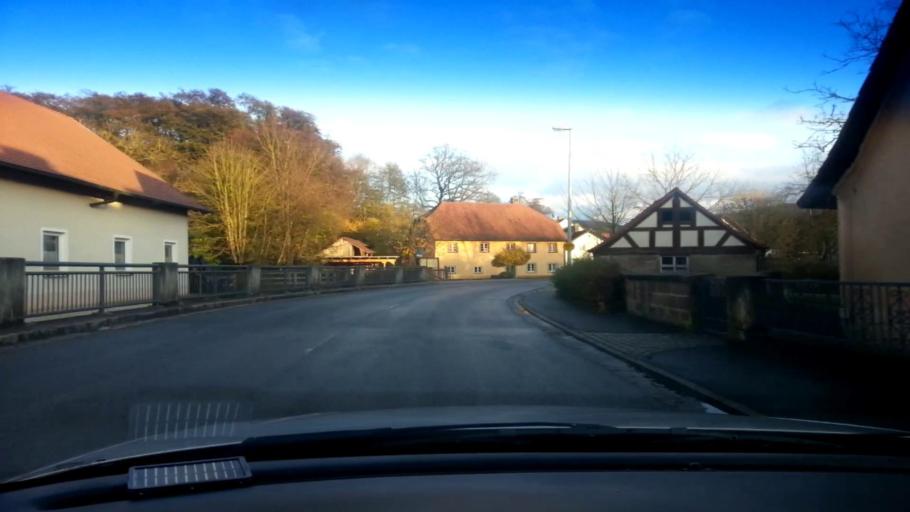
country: DE
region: Bavaria
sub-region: Upper Franconia
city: Strullendorf
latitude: 49.8586
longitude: 11.0085
